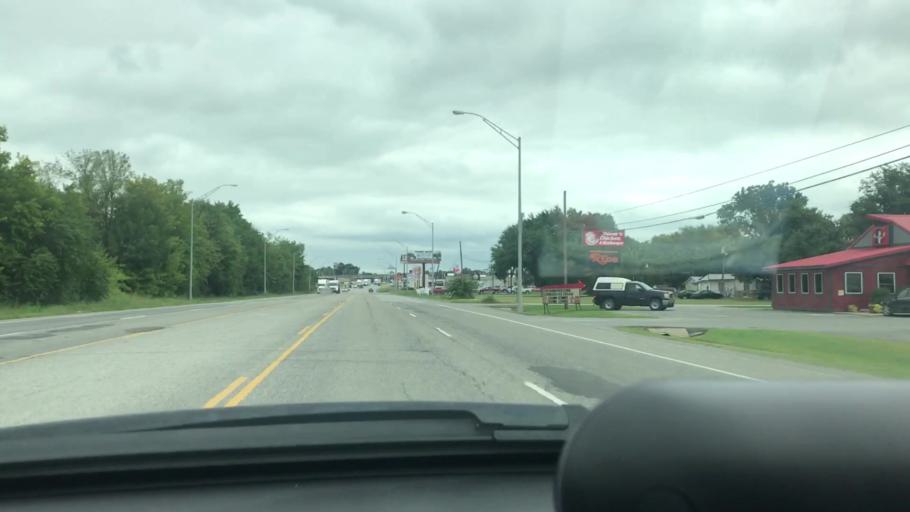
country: US
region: Oklahoma
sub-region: Wagoner County
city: Wagoner
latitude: 35.9528
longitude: -95.3952
